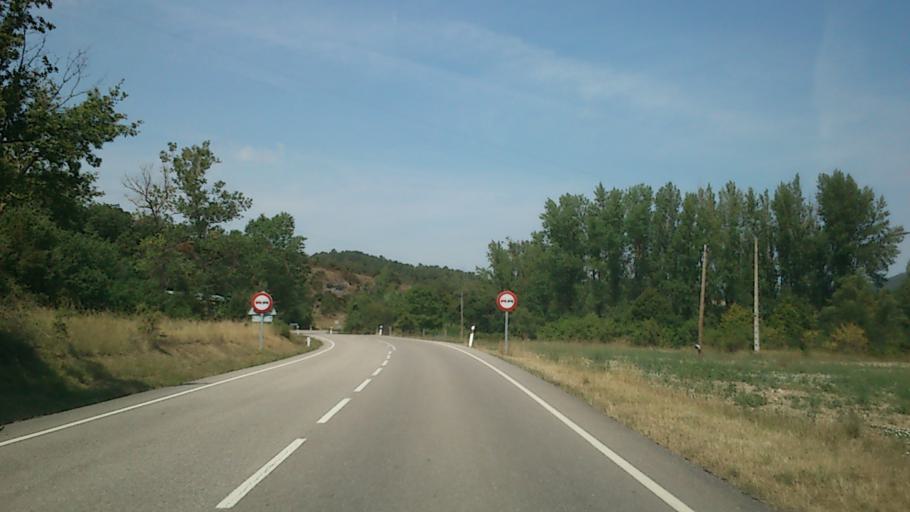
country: ES
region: Castille and Leon
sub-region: Provincia de Burgos
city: Trespaderne
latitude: 42.8568
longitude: -3.3332
